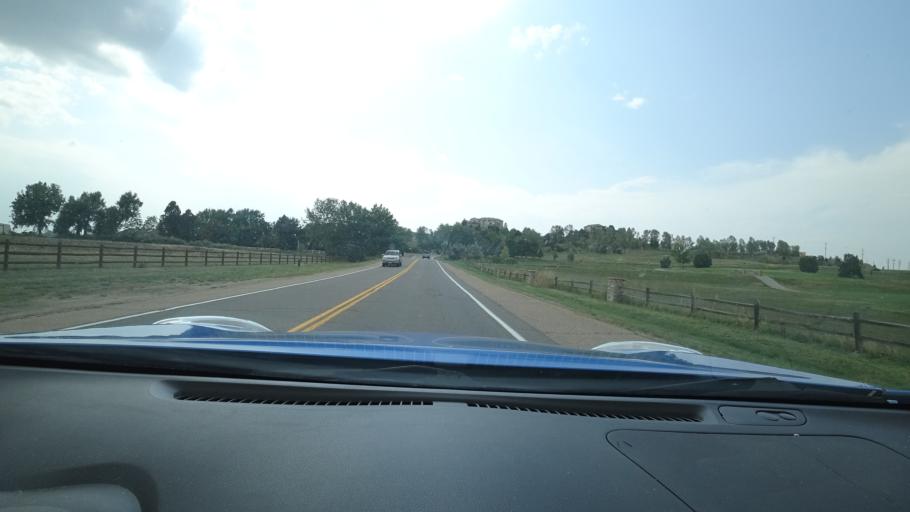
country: US
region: Colorado
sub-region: Adams County
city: Todd Creek
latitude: 39.9252
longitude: -104.8815
